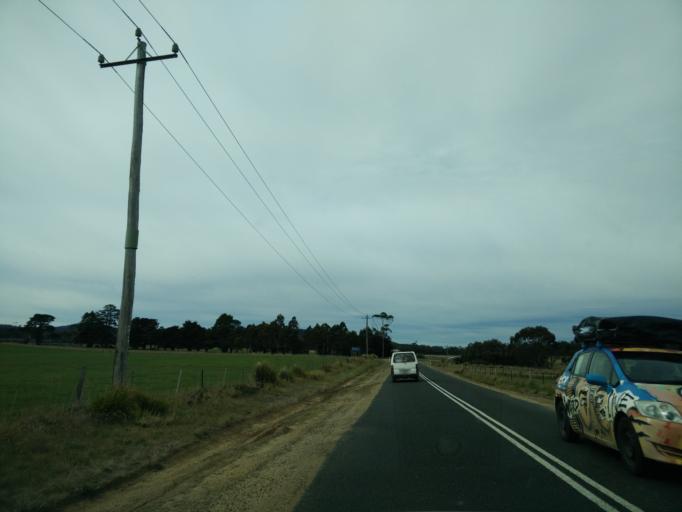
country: AU
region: Tasmania
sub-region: Break O'Day
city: St Helens
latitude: -41.9075
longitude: 148.2529
